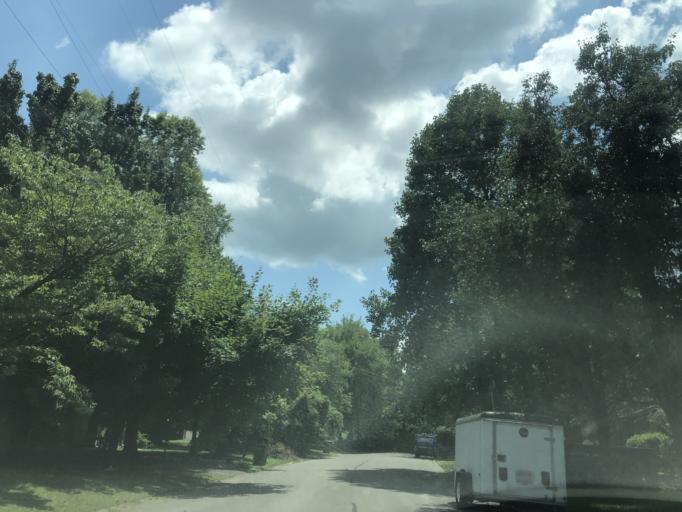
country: US
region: Tennessee
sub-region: Davidson County
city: Lakewood
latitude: 36.1954
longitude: -86.6129
